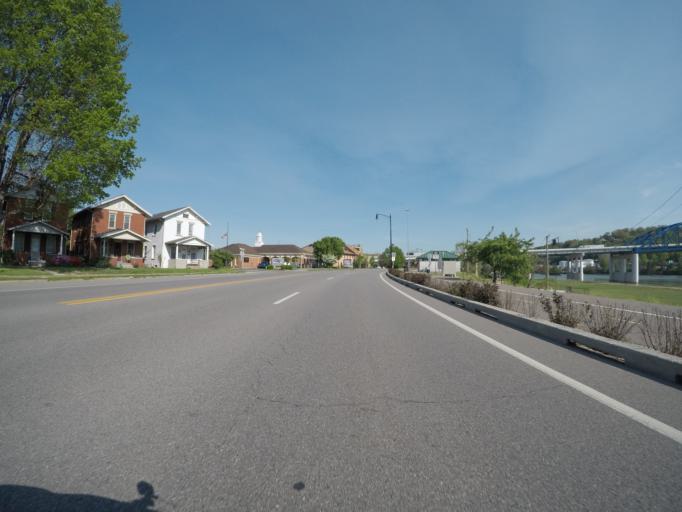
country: US
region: West Virginia
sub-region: Kanawha County
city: Charleston
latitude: 38.3578
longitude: -81.6483
